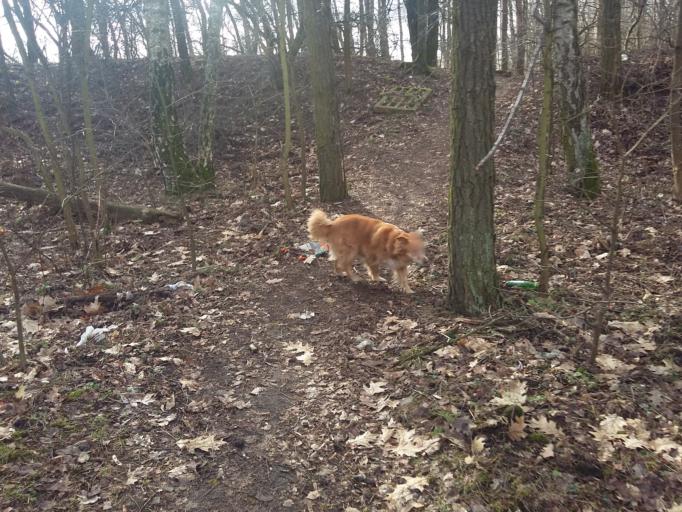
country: PL
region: Lodz Voivodeship
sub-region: Powiat pabianicki
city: Ksawerow
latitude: 51.7321
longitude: 19.4179
